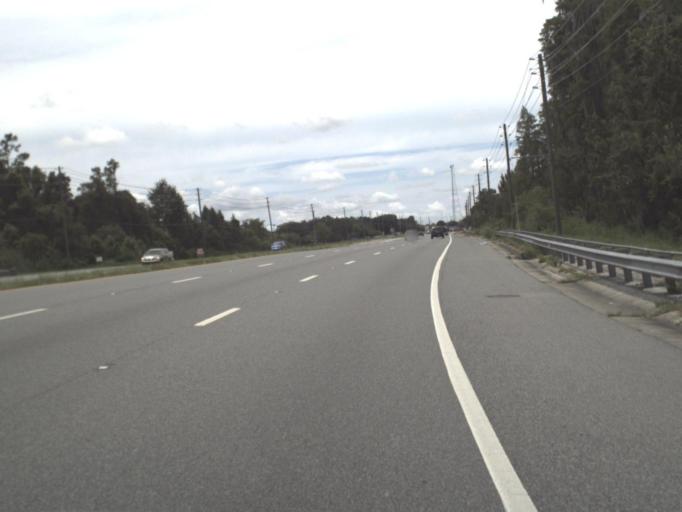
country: US
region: Florida
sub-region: Pasco County
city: Land O' Lakes
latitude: 28.1863
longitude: -82.4511
